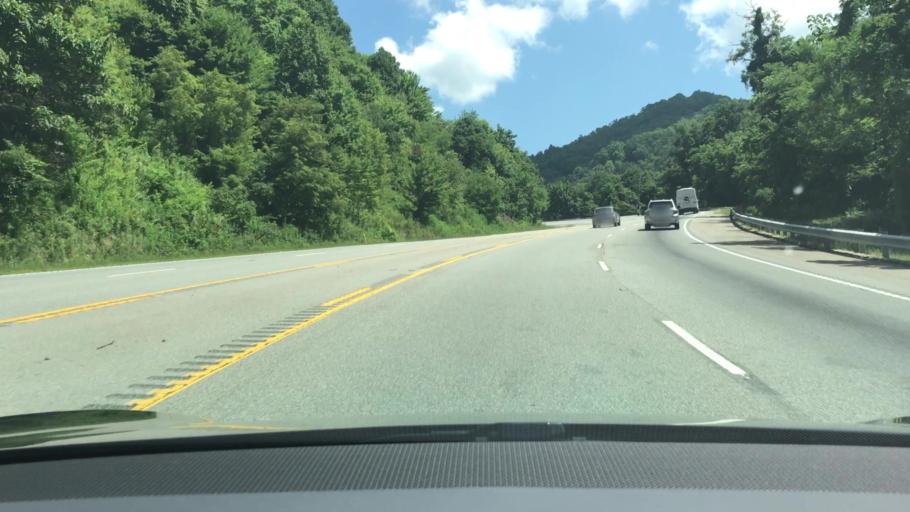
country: US
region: North Carolina
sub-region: Macon County
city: Franklin
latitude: 35.2503
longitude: -83.3177
